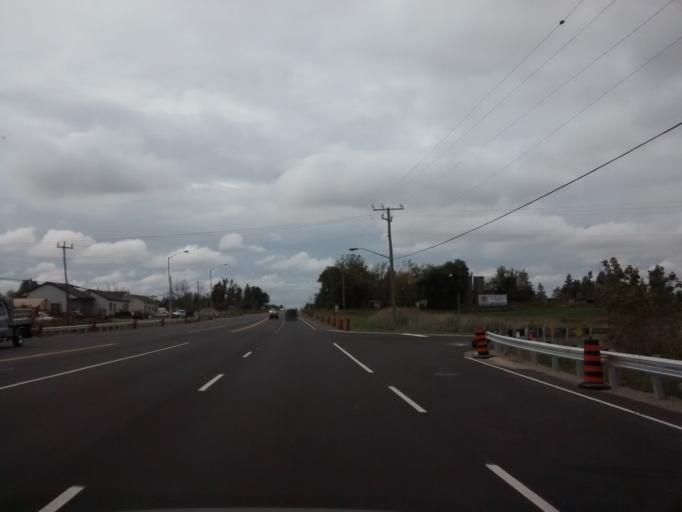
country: CA
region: Ontario
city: Ancaster
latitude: 43.1339
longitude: -79.9247
